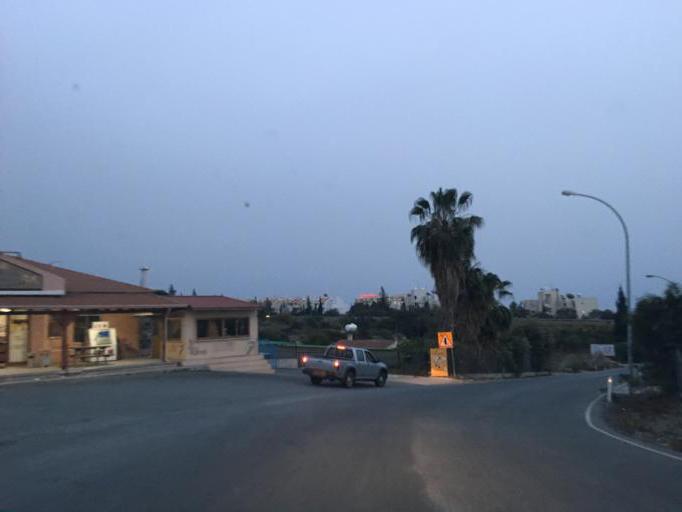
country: CY
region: Larnaka
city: Agios Tychon
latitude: 34.7173
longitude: 33.1633
